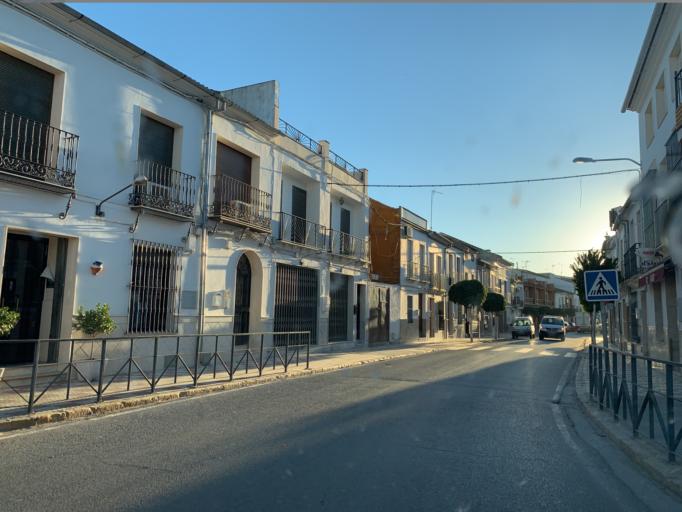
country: ES
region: Andalusia
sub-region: Provincia de Sevilla
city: Pedrera
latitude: 37.2227
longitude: -4.8937
